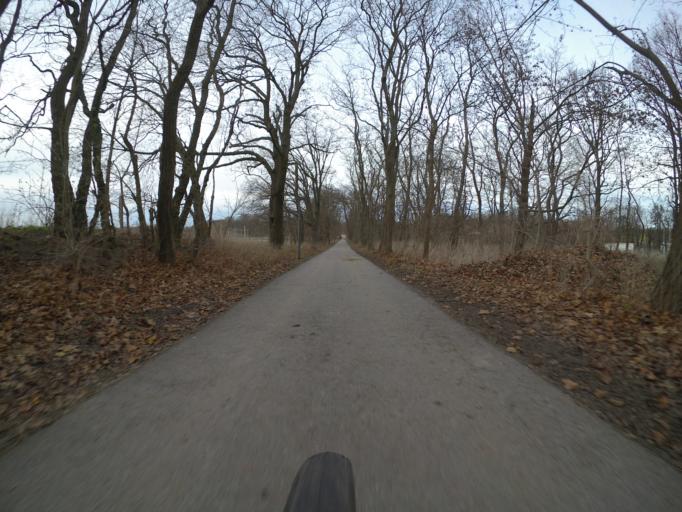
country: DE
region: Brandenburg
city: Hoppegarten
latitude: 52.4987
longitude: 13.6653
